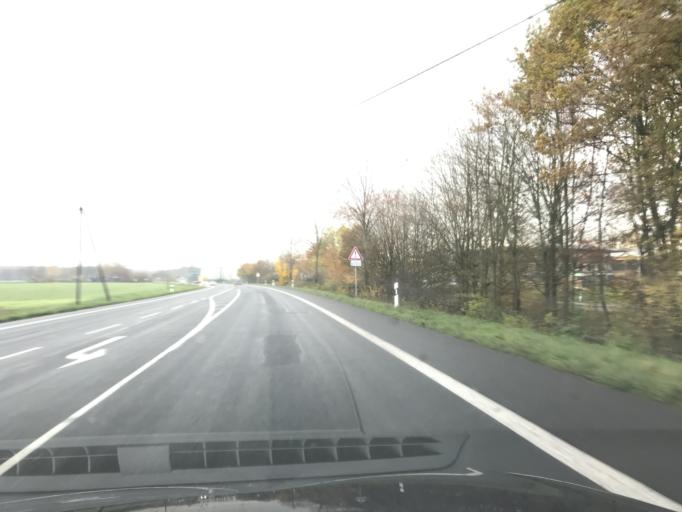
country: DE
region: North Rhine-Westphalia
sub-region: Regierungsbezirk Munster
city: Everswinkel
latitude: 51.9286
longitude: 7.8668
